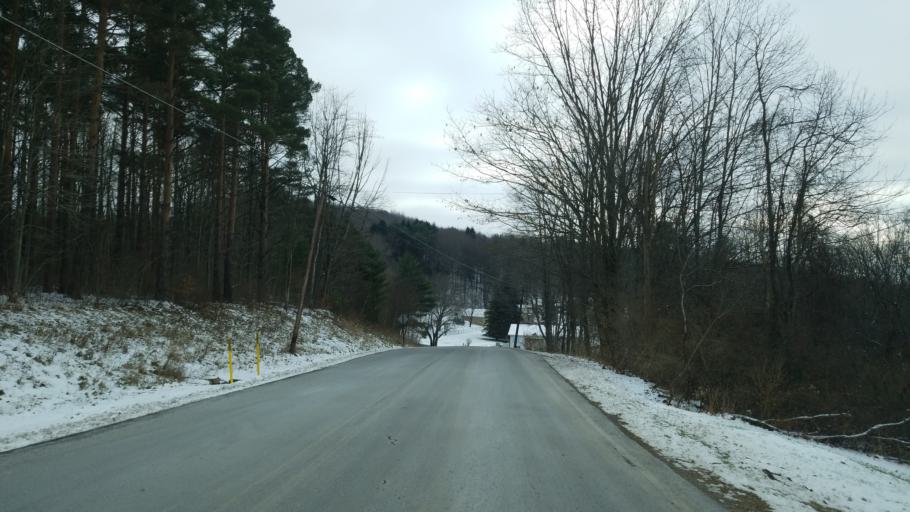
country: US
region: Pennsylvania
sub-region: Clearfield County
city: Sandy
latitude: 41.0865
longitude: -78.7499
